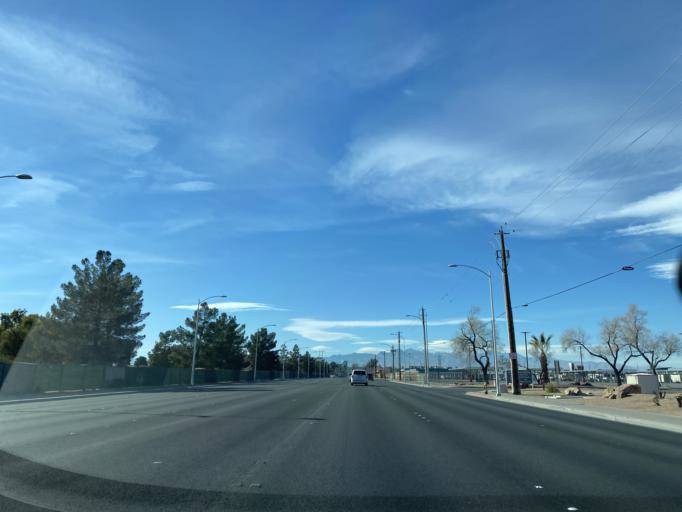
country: US
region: Nevada
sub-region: Clark County
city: North Las Vegas
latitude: 36.1736
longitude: -115.1009
